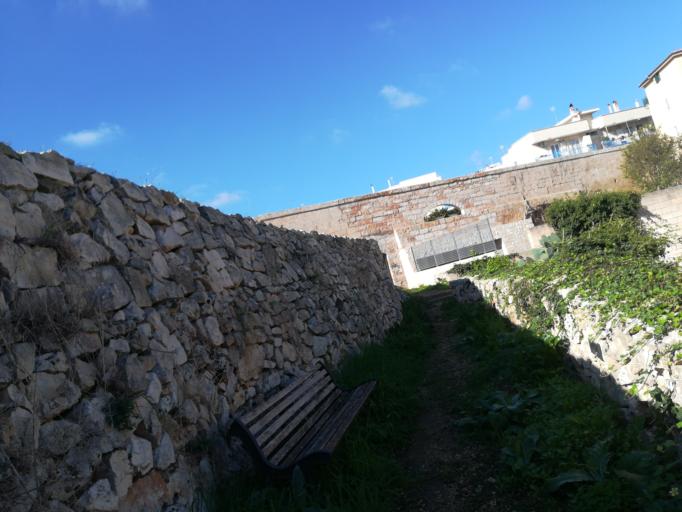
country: IT
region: Apulia
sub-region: Provincia di Bari
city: Polignano a Mare
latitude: 40.9949
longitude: 17.2163
